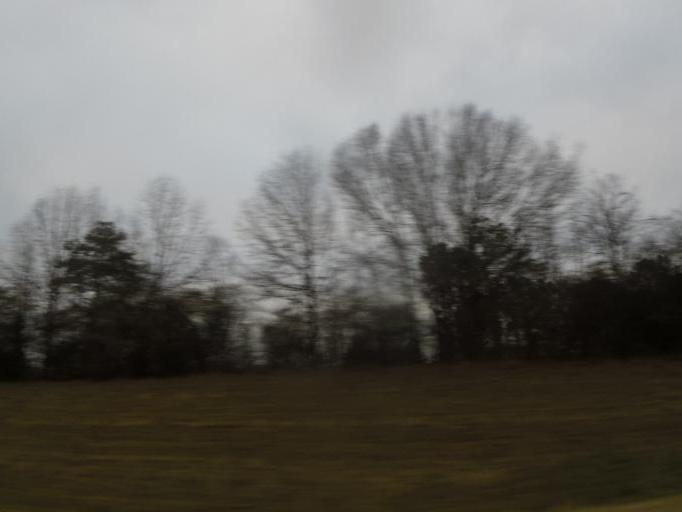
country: US
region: Alabama
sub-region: Blount County
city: Smoke Rise
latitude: 33.9642
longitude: -86.8668
